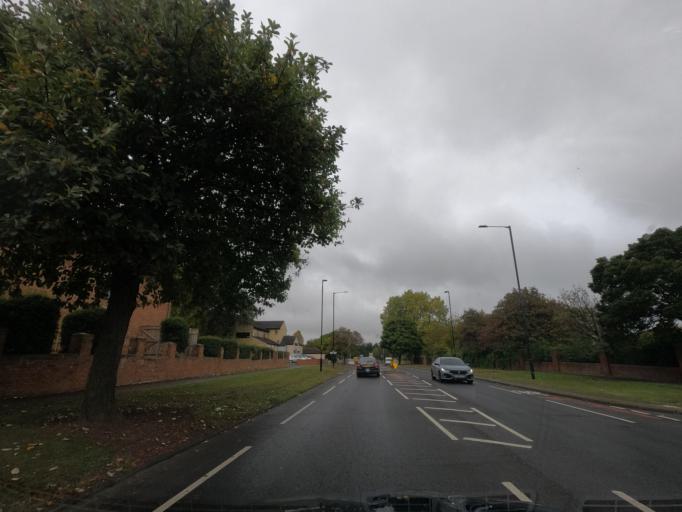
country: GB
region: England
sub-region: Middlesbrough
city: Nunthorpe
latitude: 54.5622
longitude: -1.1906
